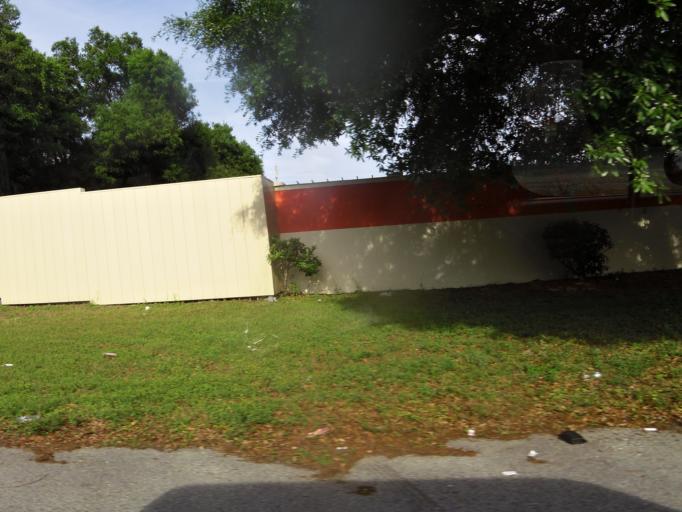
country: US
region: Florida
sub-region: Duval County
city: Jacksonville
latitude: 30.3289
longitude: -81.5927
